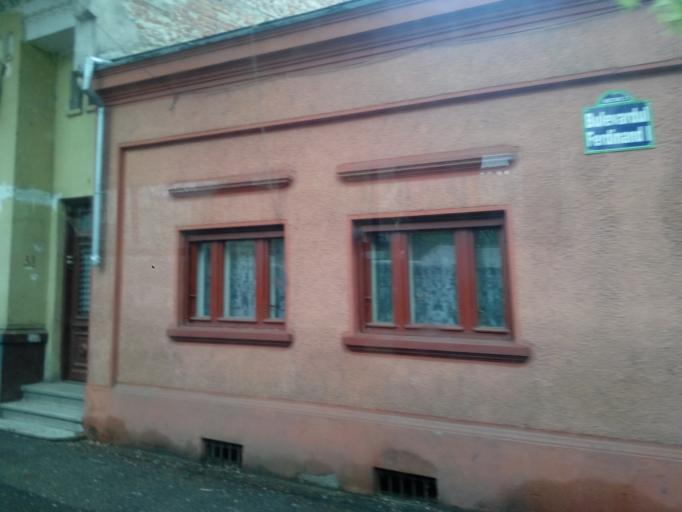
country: RO
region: Bucuresti
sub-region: Municipiul Bucuresti
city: Bucharest
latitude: 44.4406
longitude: 26.1219
